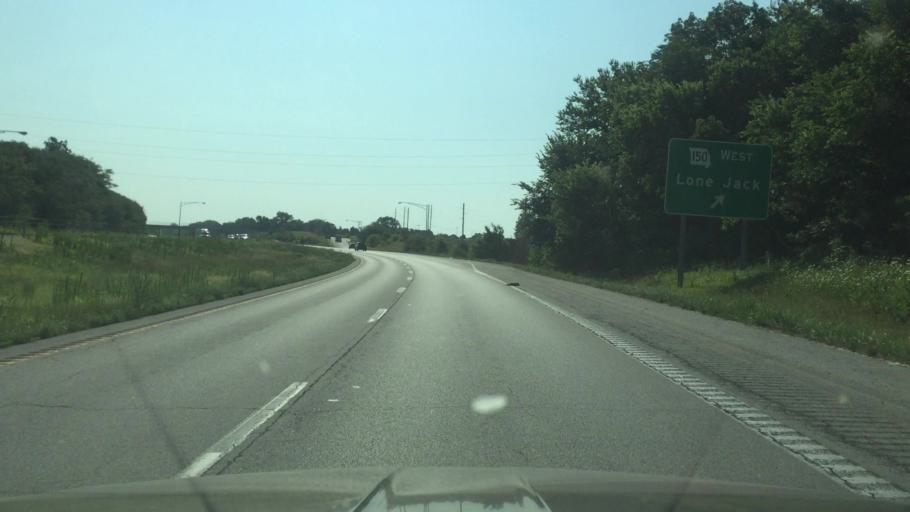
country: US
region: Missouri
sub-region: Jackson County
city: Lone Jack
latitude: 38.8683
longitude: -94.1789
